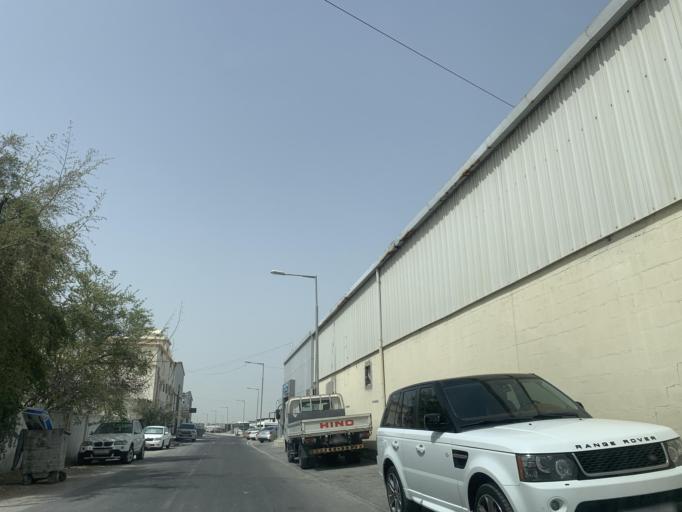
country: BH
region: Northern
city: Madinat `Isa
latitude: 26.1859
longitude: 50.5247
